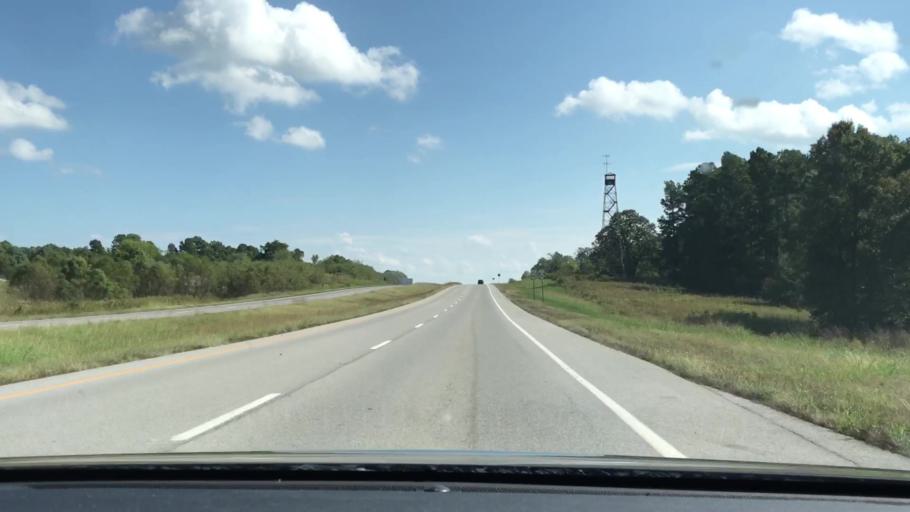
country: US
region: Kentucky
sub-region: Trigg County
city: Cadiz
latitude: 36.7802
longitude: -88.0601
